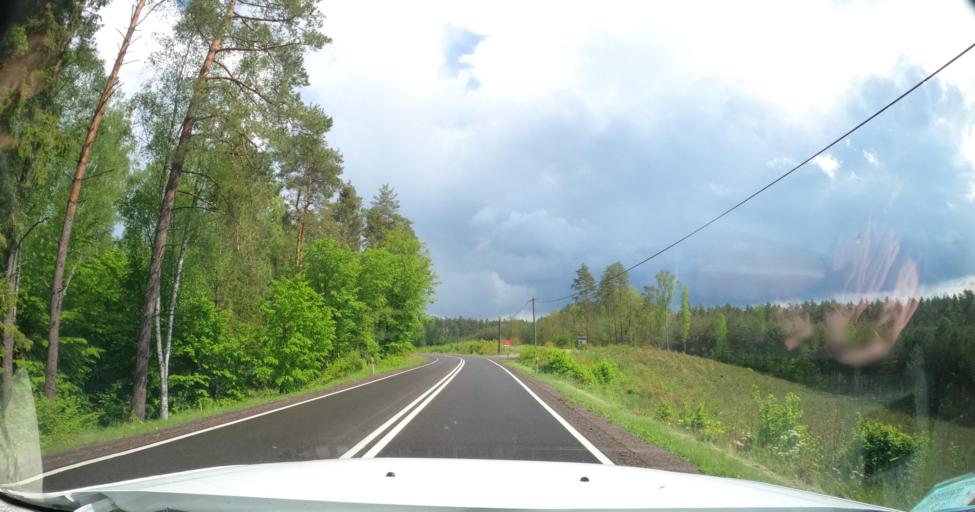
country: PL
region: Pomeranian Voivodeship
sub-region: Powiat bytowski
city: Czarna Dabrowka
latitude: 54.3407
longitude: 17.6121
